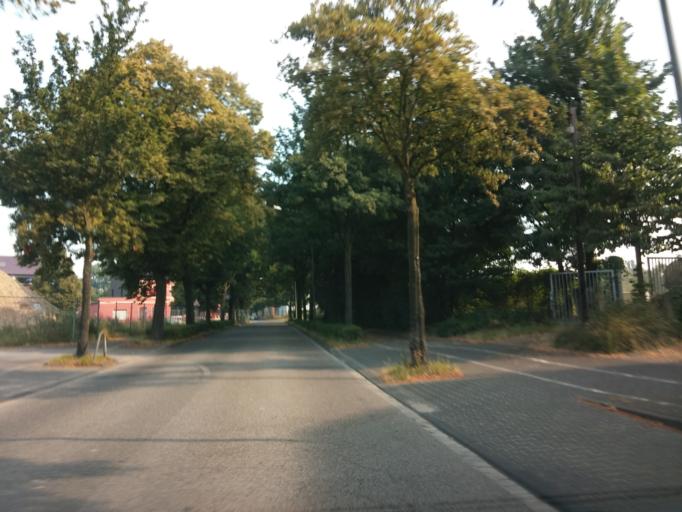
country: DE
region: North Rhine-Westphalia
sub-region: Regierungsbezirk Munster
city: Bottrop
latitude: 51.5241
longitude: 6.9756
